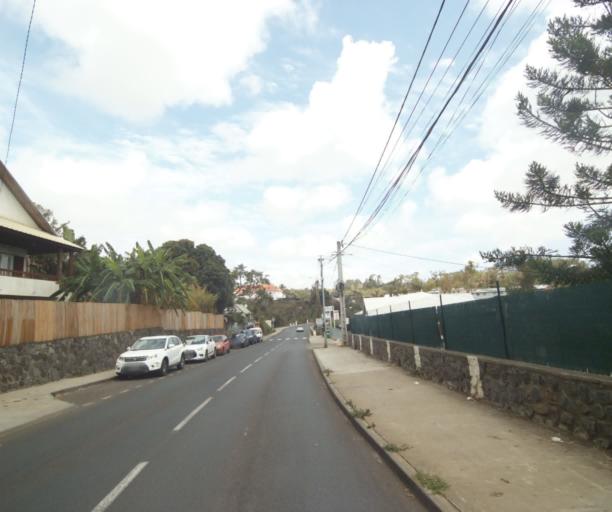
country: RE
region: Reunion
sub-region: Reunion
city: Saint-Paul
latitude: -21.0511
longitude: 55.2675
